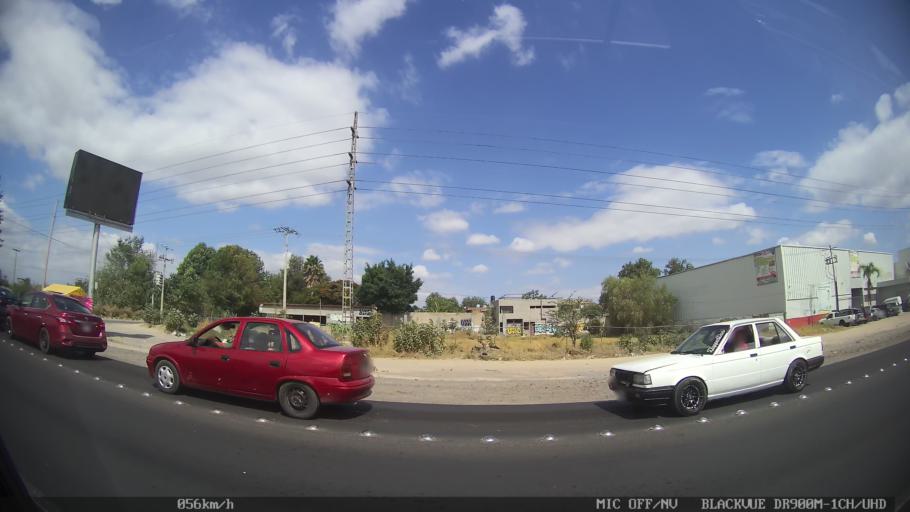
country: MX
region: Jalisco
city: Tonala
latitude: 20.6543
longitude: -103.2342
